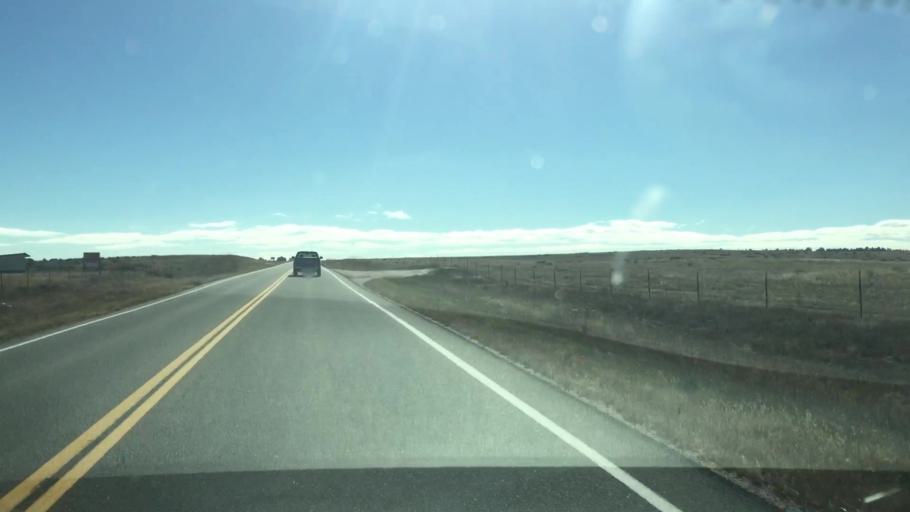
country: US
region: Colorado
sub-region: Elbert County
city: Kiowa
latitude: 39.3391
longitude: -104.4336
